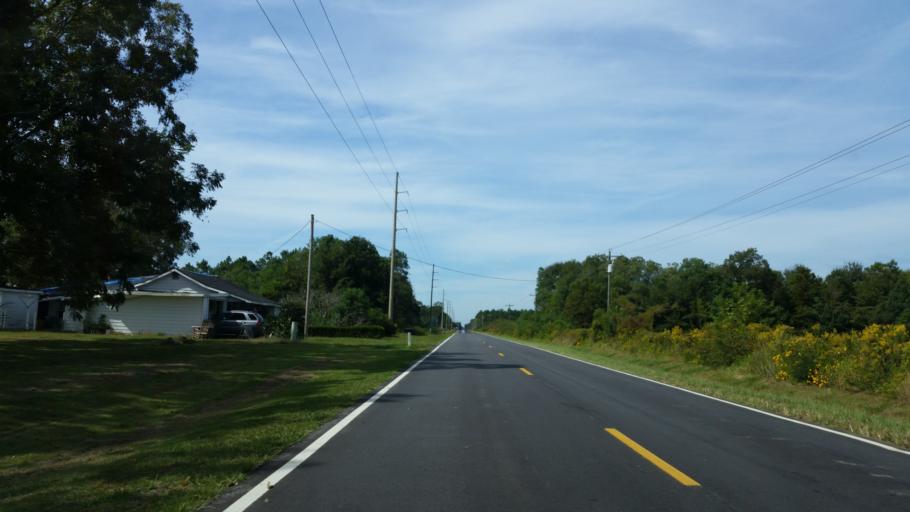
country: US
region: Alabama
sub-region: Baldwin County
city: Loxley
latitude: 30.6332
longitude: -87.6851
